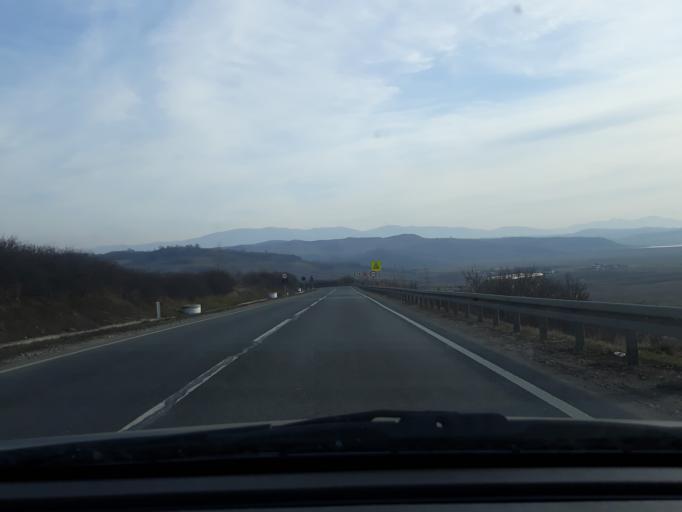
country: RO
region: Salaj
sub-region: Comuna Varsolt
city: Varsolt
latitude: 47.2132
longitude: 22.9293
